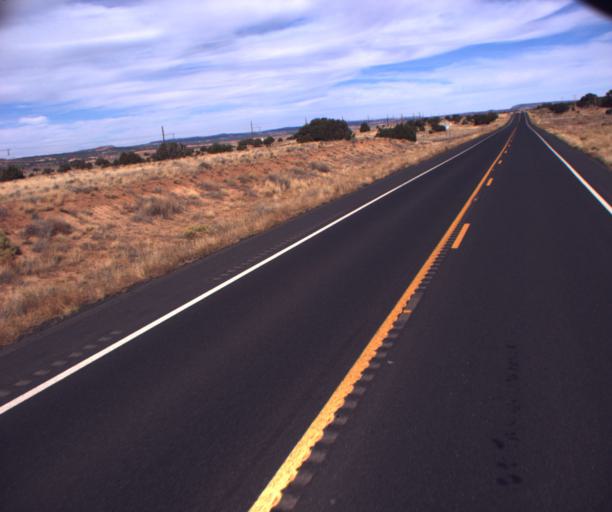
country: US
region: Arizona
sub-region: Navajo County
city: Kayenta
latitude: 36.4980
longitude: -110.6215
